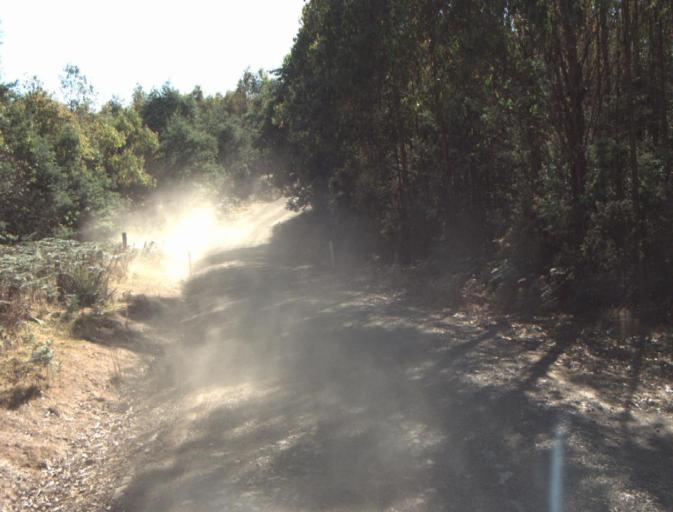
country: AU
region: Tasmania
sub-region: Dorset
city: Scottsdale
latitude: -41.2739
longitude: 147.3724
